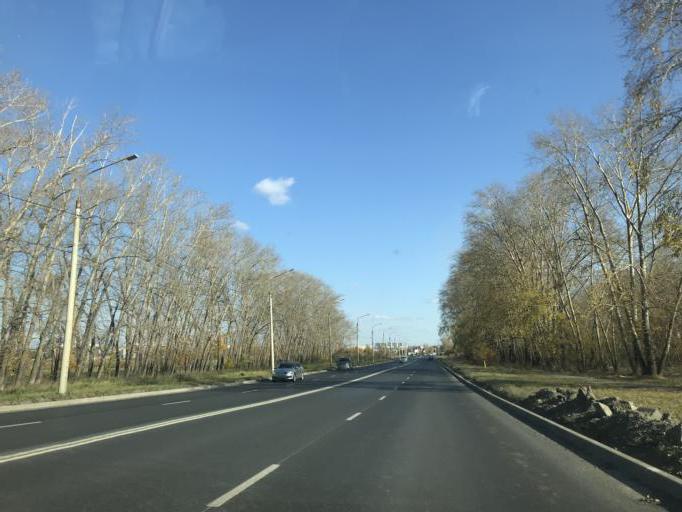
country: RU
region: Chelyabinsk
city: Roshchino
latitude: 55.2401
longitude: 61.3372
